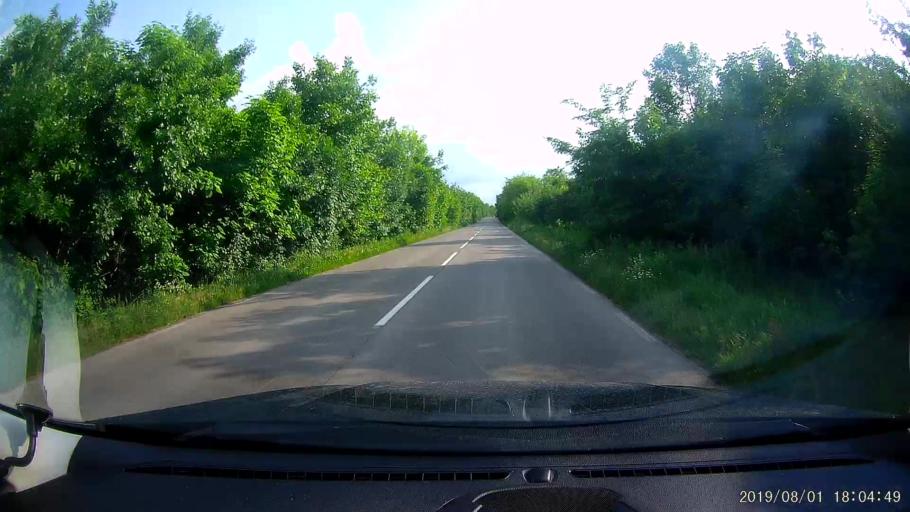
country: BG
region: Silistra
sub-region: Obshtina Alfatar
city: Alfatar
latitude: 43.9018
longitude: 27.2718
